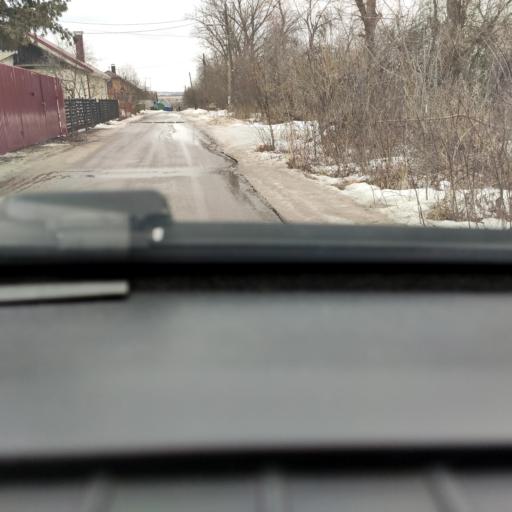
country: RU
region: Voronezj
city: Strelitsa
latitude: 51.6048
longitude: 38.9092
